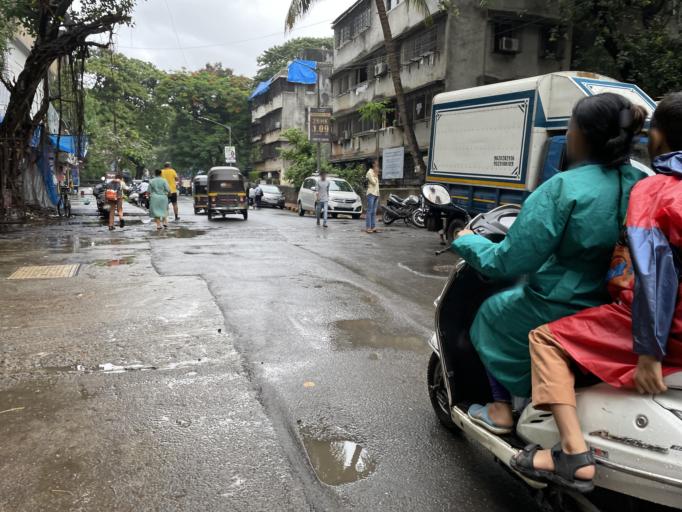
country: IN
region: Maharashtra
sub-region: Mumbai Suburban
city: Borivli
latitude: 19.2526
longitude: 72.8601
